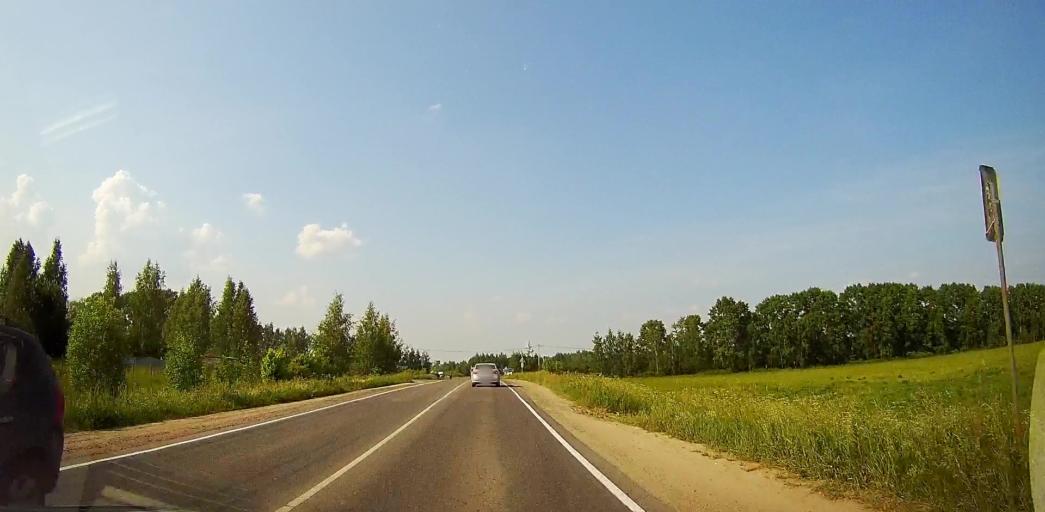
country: RU
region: Moskovskaya
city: Zhitnevo
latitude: 55.3195
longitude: 37.9001
